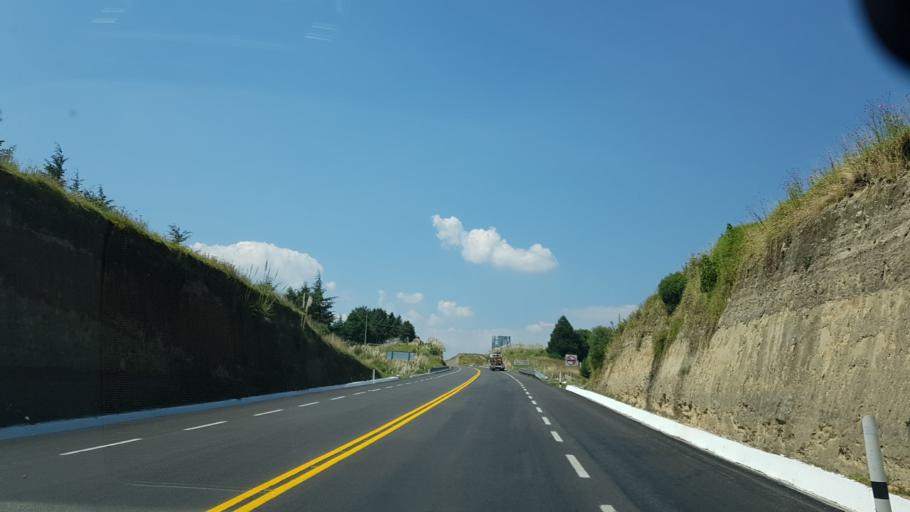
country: MX
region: Mexico
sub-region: Almoloya de Juarez
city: San Pedro de la Hortaliza (Ejido Almoloyan)
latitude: 19.3786
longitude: -99.8533
